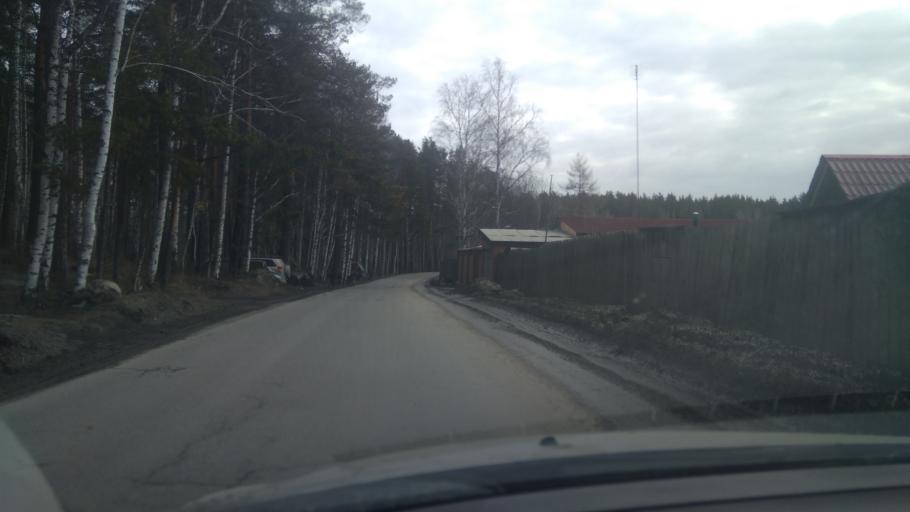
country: RU
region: Sverdlovsk
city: Severka
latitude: 56.8428
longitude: 60.3846
